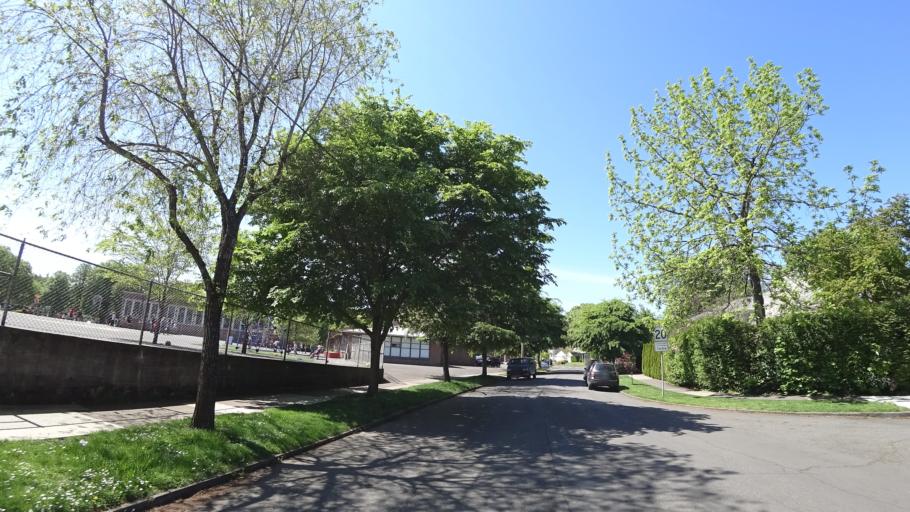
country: US
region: Oregon
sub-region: Clackamas County
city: Milwaukie
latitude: 45.4687
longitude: -122.6274
